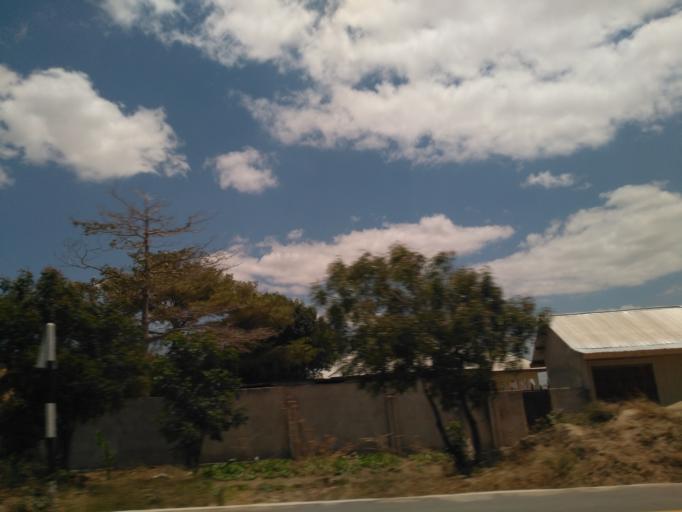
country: TZ
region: Dodoma
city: Kisasa
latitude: -6.1728
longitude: 35.7977
